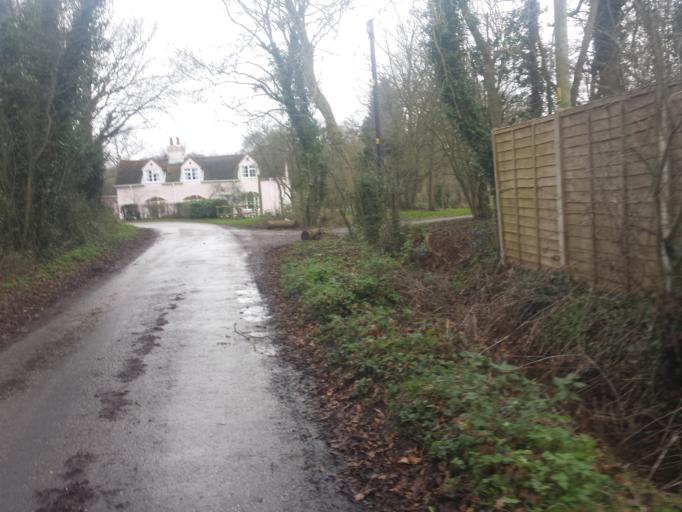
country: GB
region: England
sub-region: Essex
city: Great Bentley
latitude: 51.8893
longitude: 1.0388
